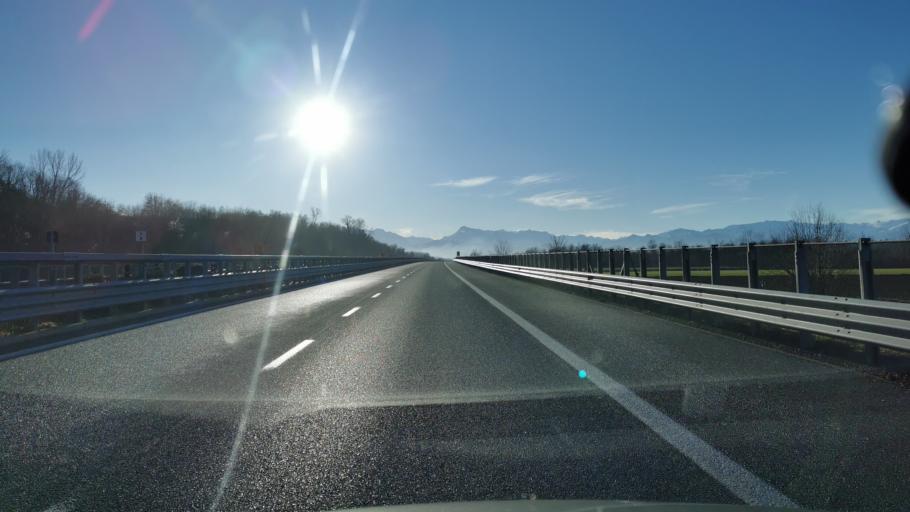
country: IT
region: Piedmont
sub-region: Provincia di Cuneo
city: Montanera
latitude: 44.4552
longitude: 7.6513
